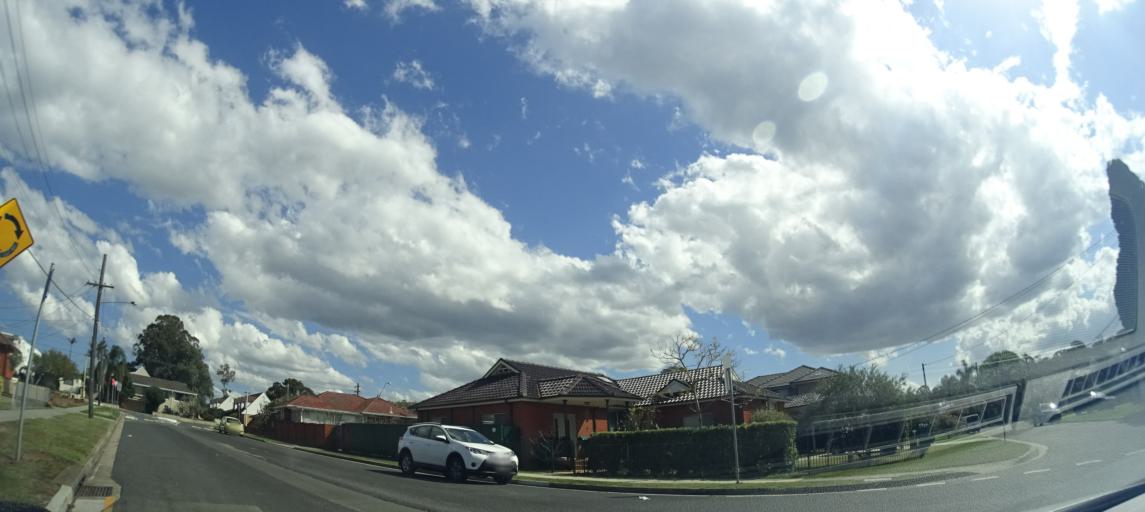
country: AU
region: New South Wales
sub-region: Bankstown
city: Revesby
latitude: -33.9541
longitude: 151.0118
